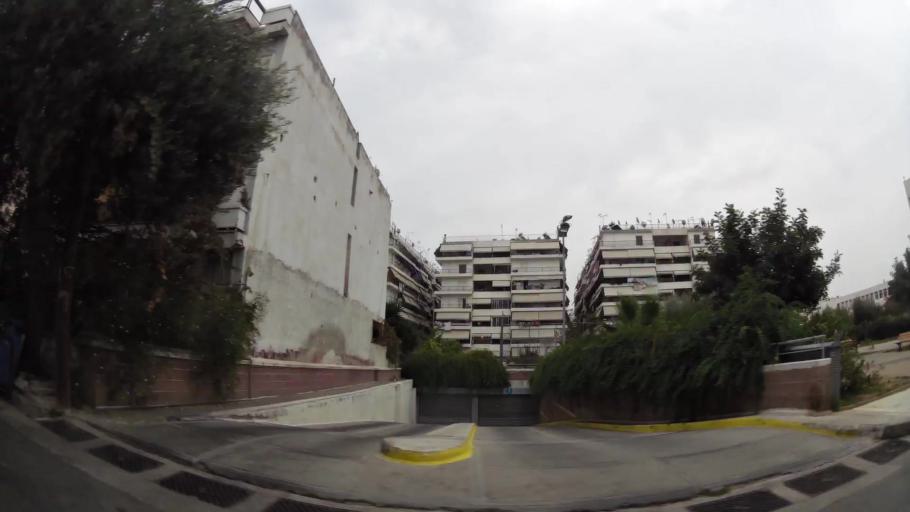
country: GR
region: Attica
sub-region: Nomos Piraios
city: Agios Ioannis Rentis
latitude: 37.9597
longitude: 23.6706
